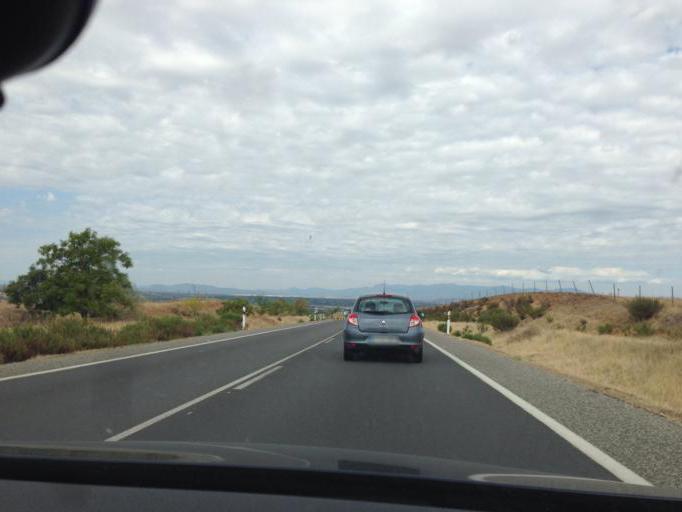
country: ES
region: Madrid
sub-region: Provincia de Madrid
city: Cobena
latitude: 40.5714
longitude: -3.5237
